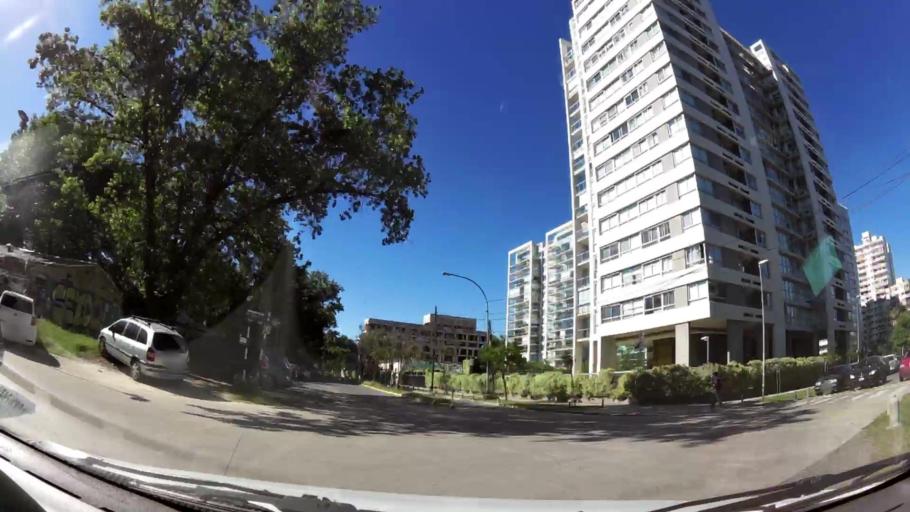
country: AR
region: Buenos Aires
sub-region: Partido de Vicente Lopez
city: Olivos
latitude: -34.5161
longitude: -58.4739
